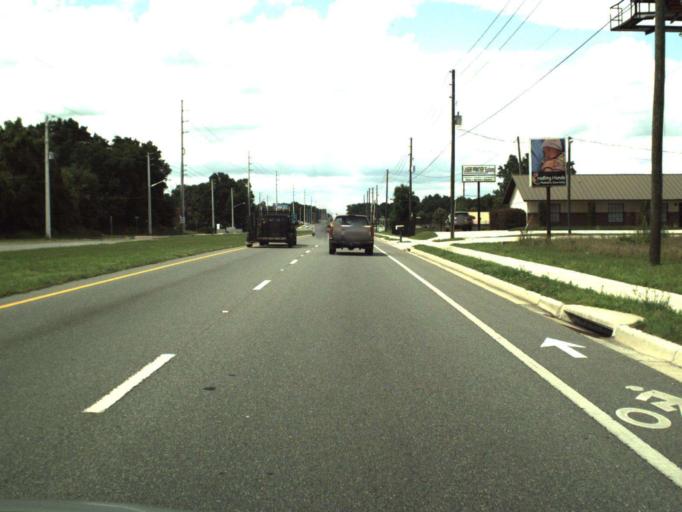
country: US
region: Florida
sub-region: Marion County
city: Silver Springs Shores
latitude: 29.1647
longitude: -82.0535
